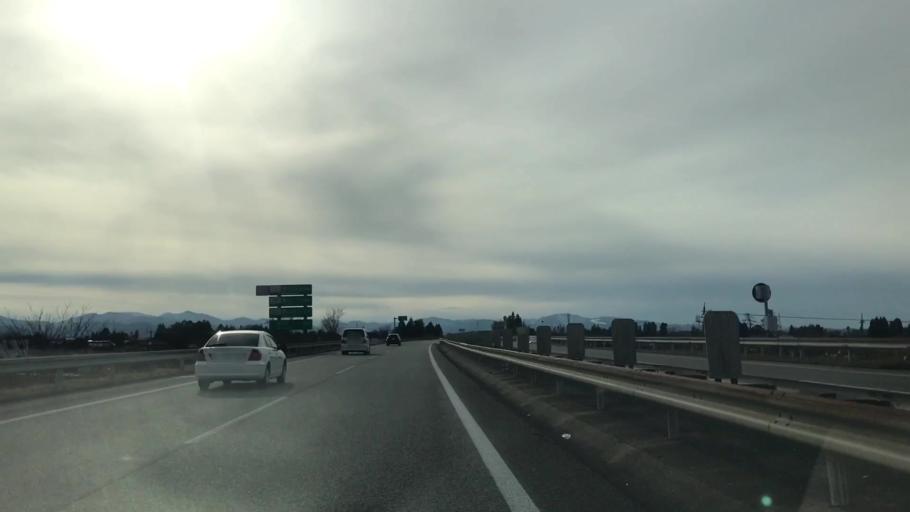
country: JP
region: Toyama
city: Kamiichi
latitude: 36.6783
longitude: 137.3172
